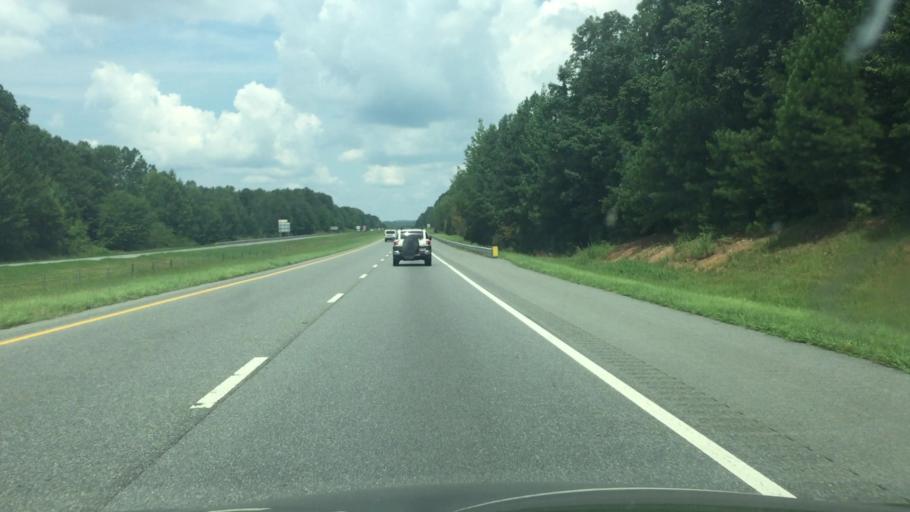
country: US
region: North Carolina
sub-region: Randolph County
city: Asheboro
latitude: 35.5436
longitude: -79.7944
